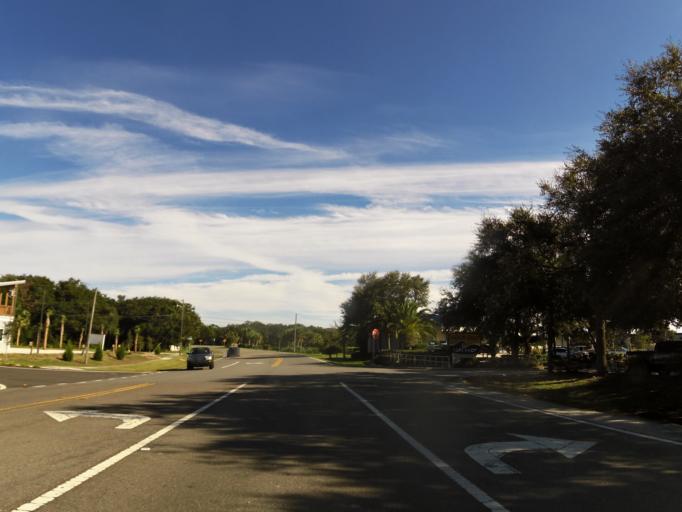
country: US
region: Florida
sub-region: Saint Johns County
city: Saint Augustine Beach
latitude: 29.8622
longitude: -81.2809
